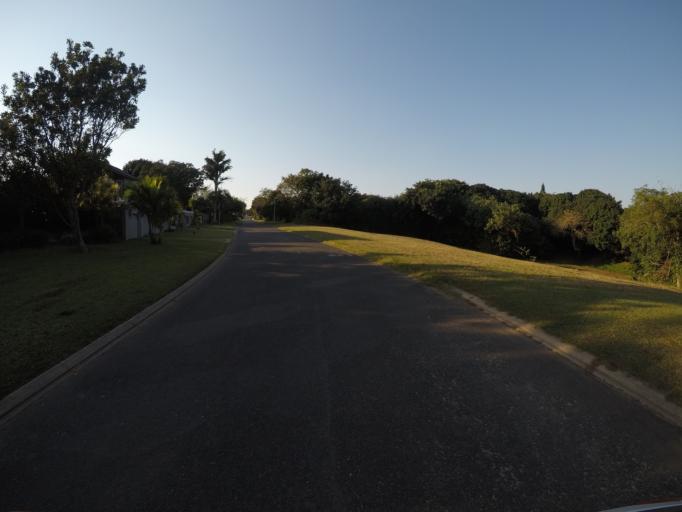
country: ZA
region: KwaZulu-Natal
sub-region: uThungulu District Municipality
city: Richards Bay
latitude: -28.7721
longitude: 32.1145
